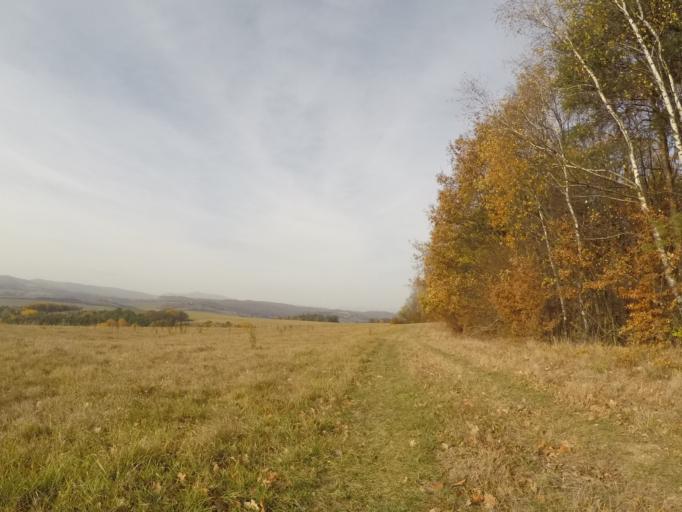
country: SK
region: Presovsky
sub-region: Okres Presov
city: Presov
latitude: 48.9227
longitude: 21.2222
